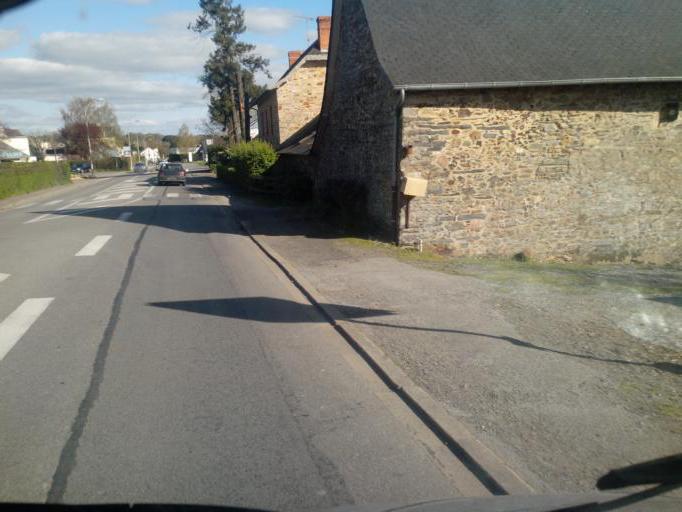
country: FR
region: Brittany
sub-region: Departement d'Ille-et-Vilaine
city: Guipry
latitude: 47.8234
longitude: -1.8372
